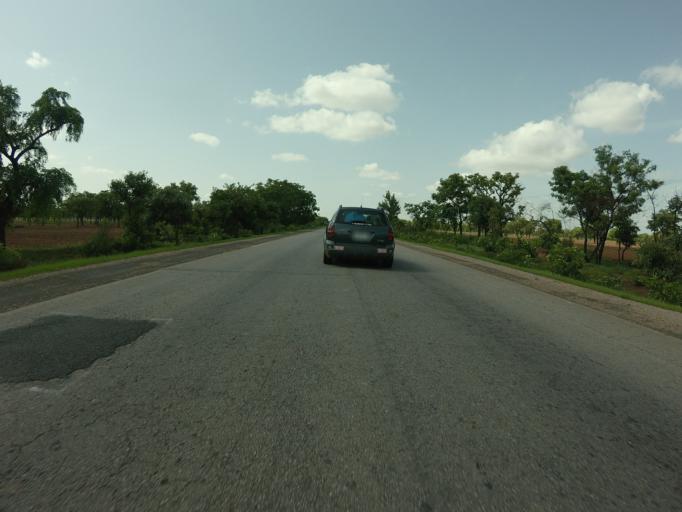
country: GH
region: Northern
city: Savelugu
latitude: 9.9437
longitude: -0.8395
